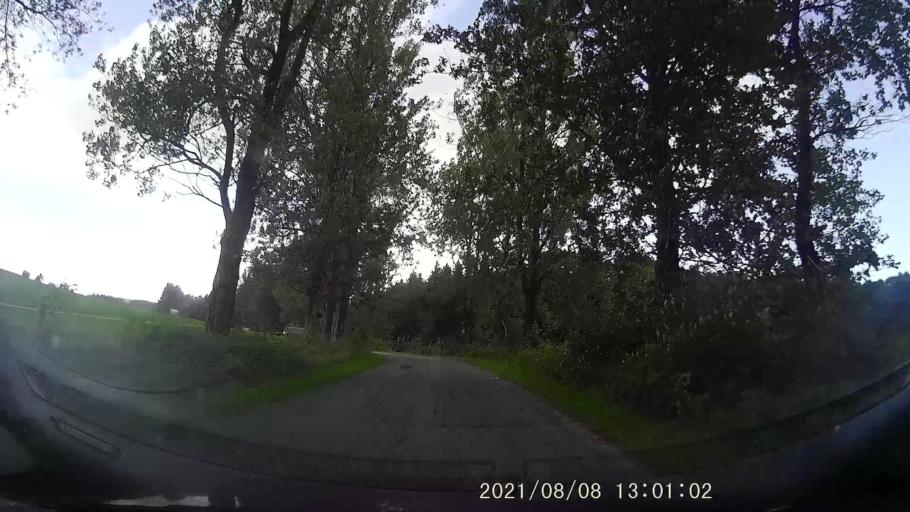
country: PL
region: Lower Silesian Voivodeship
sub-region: Powiat klodzki
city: Duszniki-Zdroj
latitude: 50.4175
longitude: 16.3420
